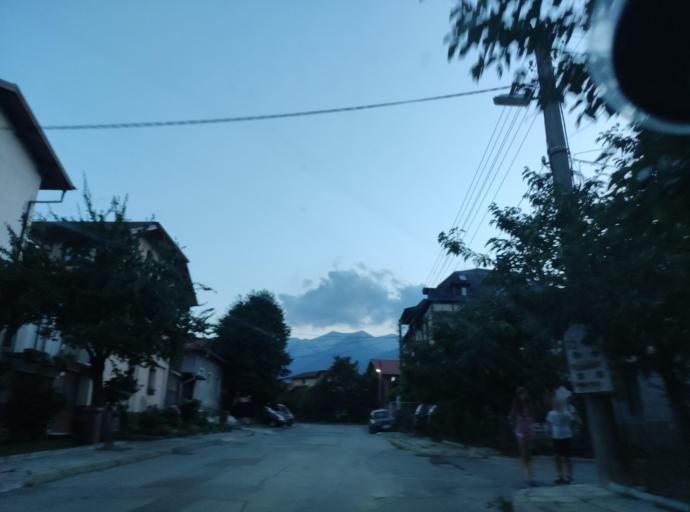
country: BG
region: Blagoevgrad
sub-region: Obshtina Bansko
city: Bansko
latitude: 41.8313
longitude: 23.4886
